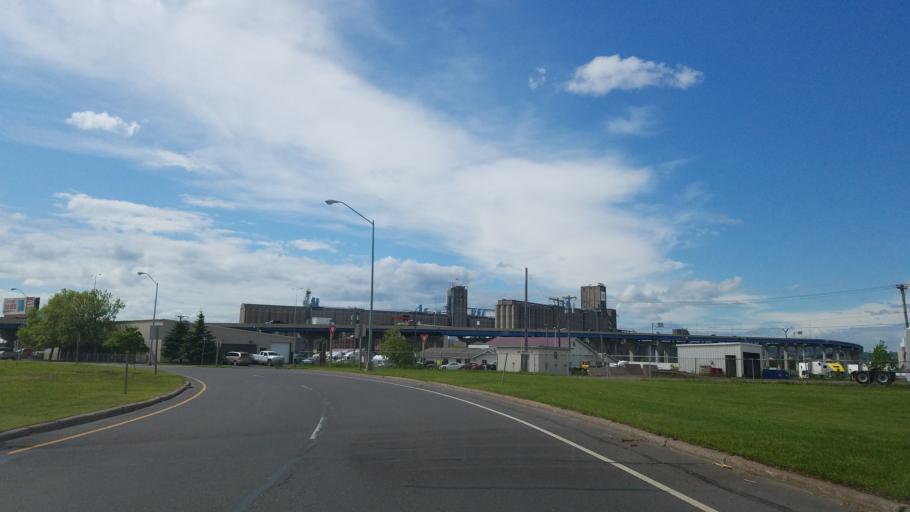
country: US
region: Wisconsin
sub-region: Douglas County
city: Superior
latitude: 46.7346
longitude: -92.0952
